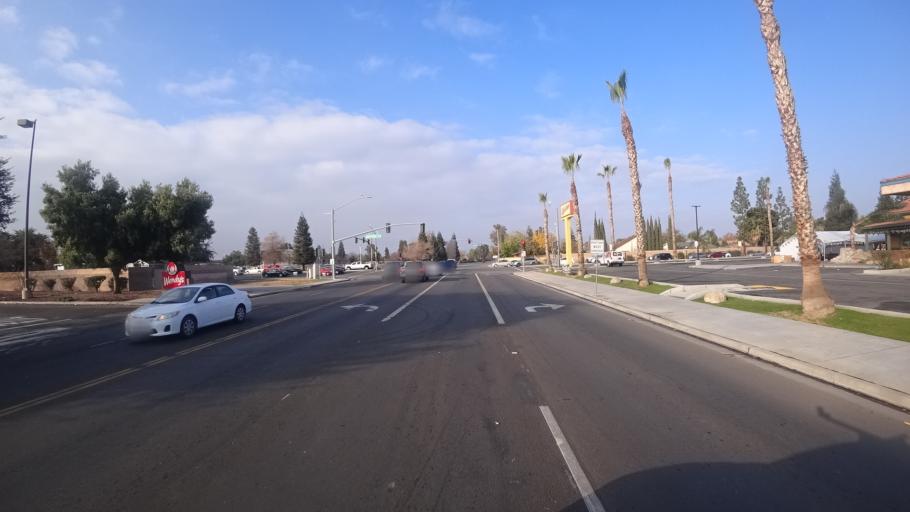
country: US
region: California
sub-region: Kern County
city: Greenacres
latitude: 35.3132
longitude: -119.0914
